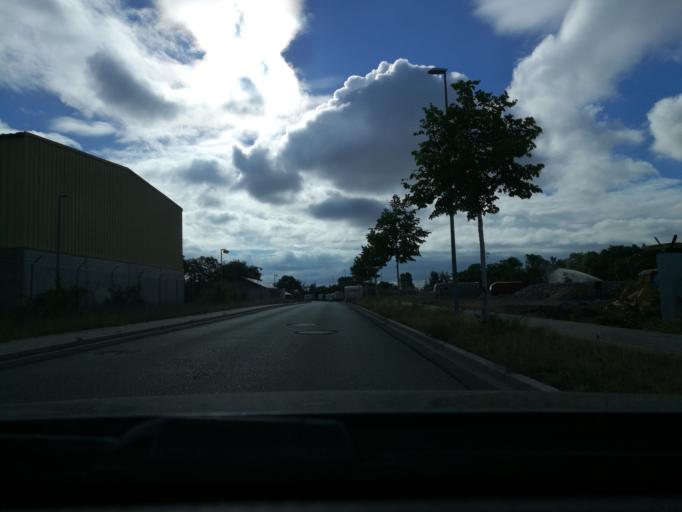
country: DE
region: Bavaria
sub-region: Regierungsbezirk Mittelfranken
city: Furth
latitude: 49.4972
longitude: 10.9599
